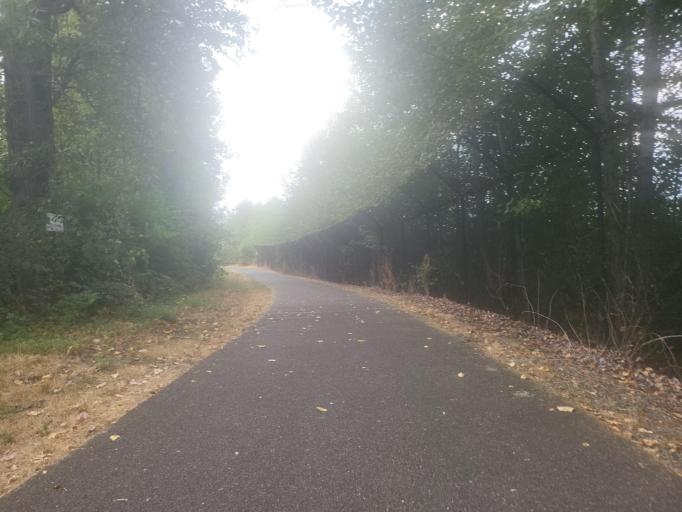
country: US
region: Washington
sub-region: King County
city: Pacific
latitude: 47.2455
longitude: -122.2354
